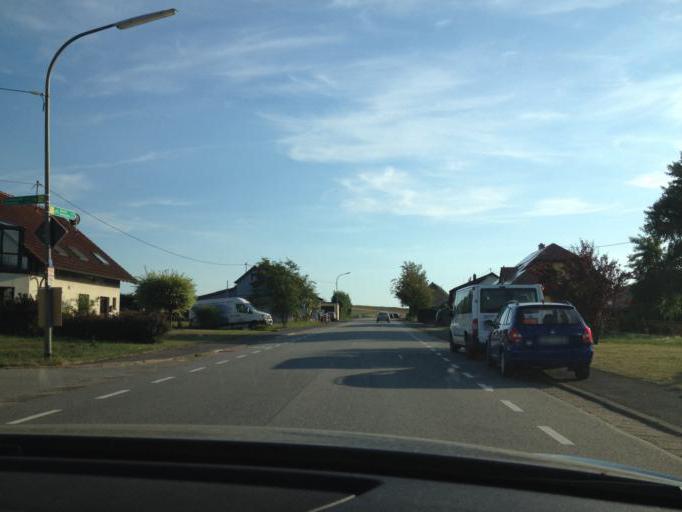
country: DE
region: Saarland
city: Oberthal
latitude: 49.5452
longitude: 7.0548
